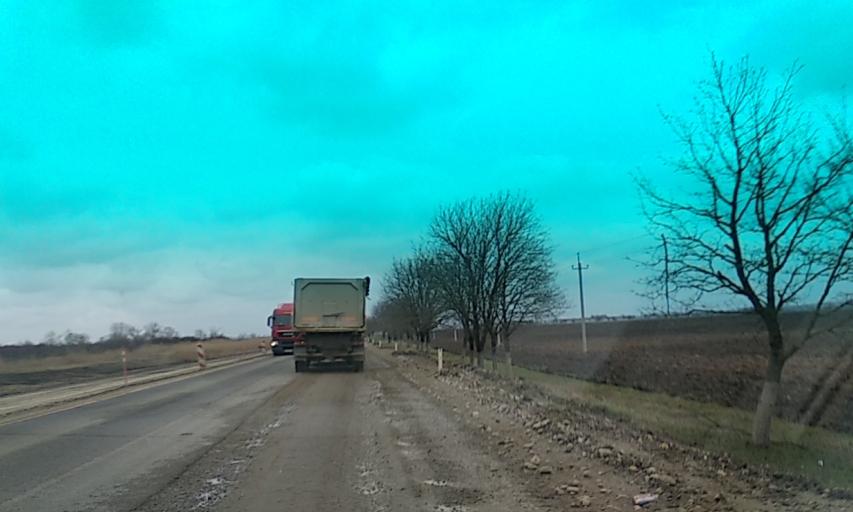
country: RU
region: Krasnodarskiy
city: Velikovechnoye
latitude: 44.9956
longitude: 39.7111
